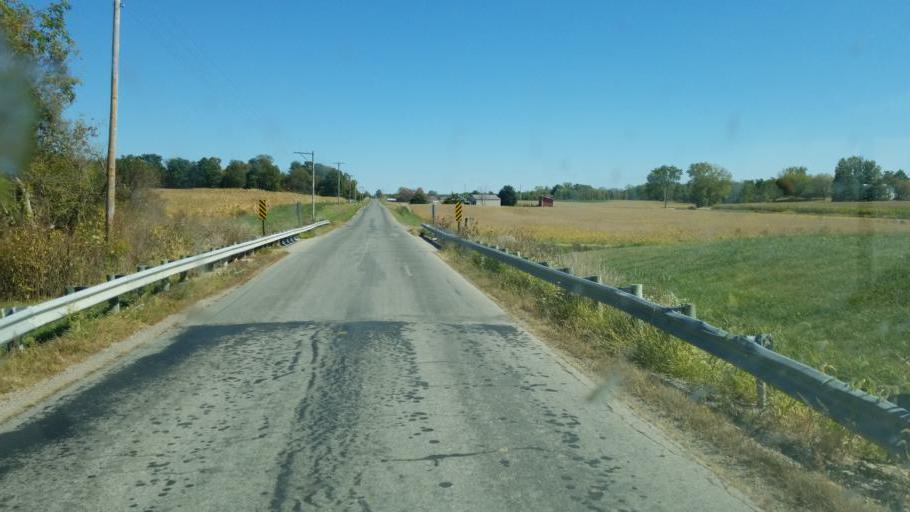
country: US
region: Ohio
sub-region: Huron County
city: Greenwich
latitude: 40.9933
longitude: -82.5234
